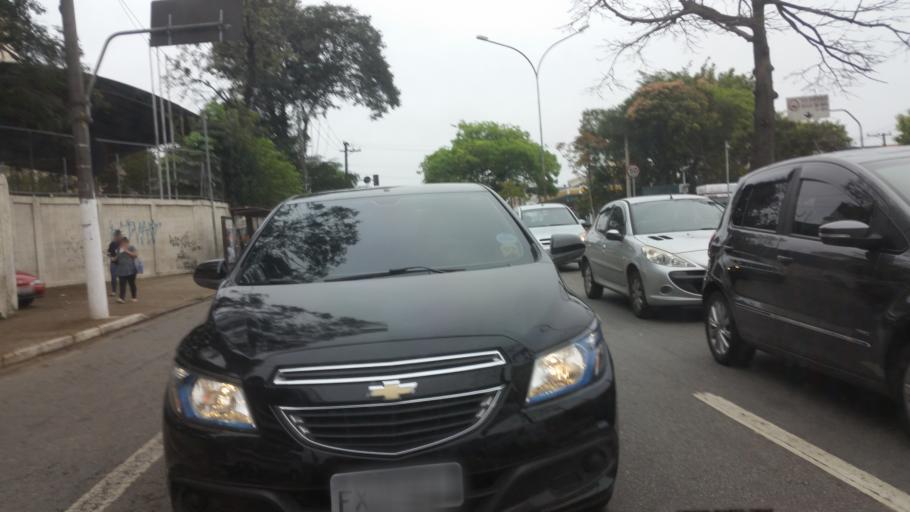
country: BR
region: Sao Paulo
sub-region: Diadema
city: Diadema
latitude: -23.6258
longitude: -46.6194
